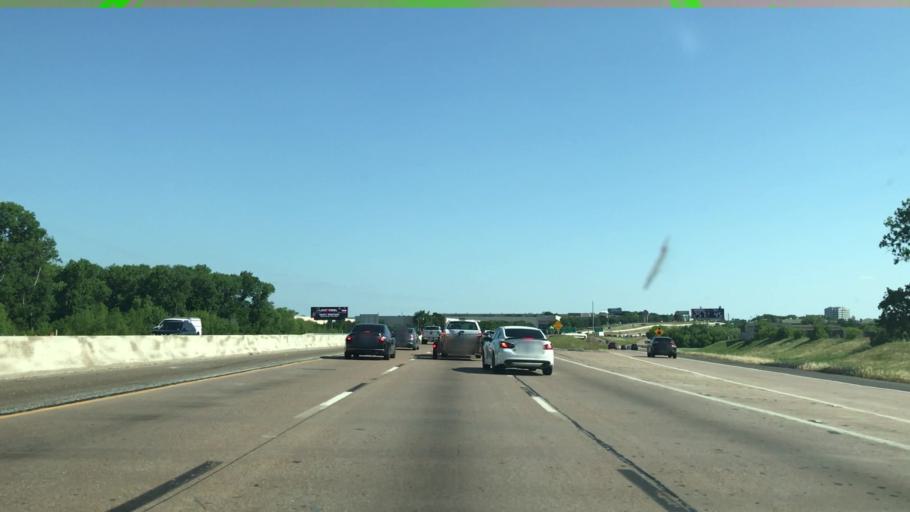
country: US
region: Texas
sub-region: Tarrant County
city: Euless
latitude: 32.8089
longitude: -97.0544
